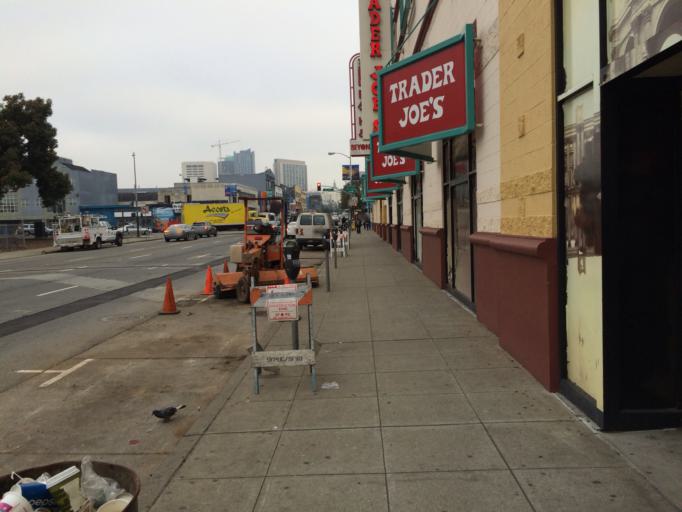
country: US
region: California
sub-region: San Francisco County
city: San Francisco
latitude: 37.7711
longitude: -122.4081
